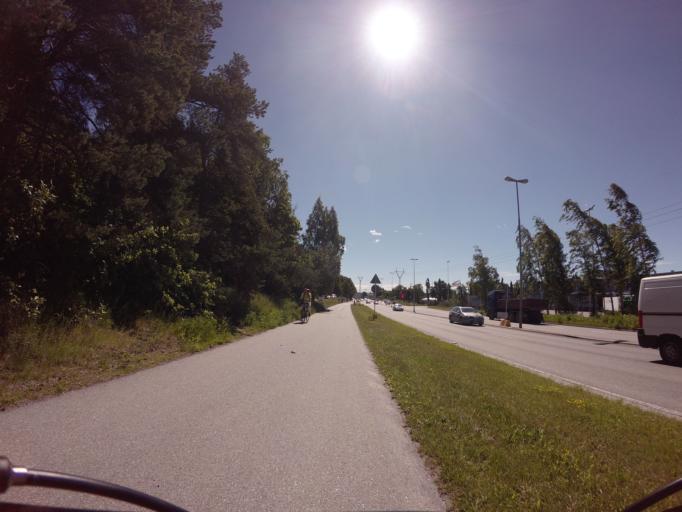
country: FI
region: Varsinais-Suomi
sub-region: Turku
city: Turku
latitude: 60.4472
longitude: 22.2197
